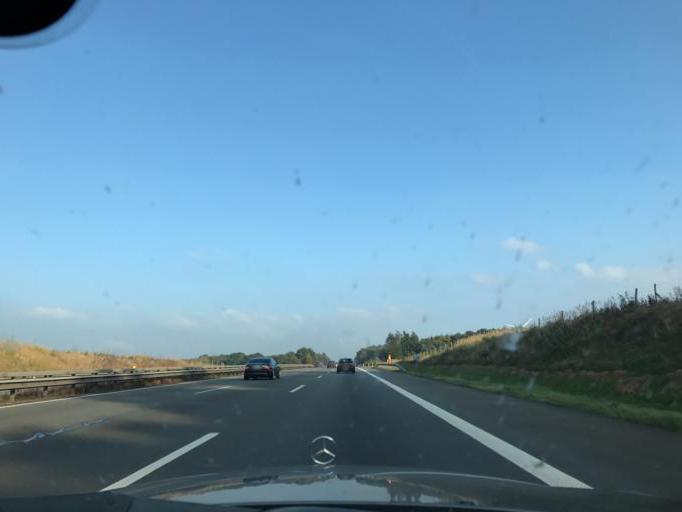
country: DE
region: Lower Saxony
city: Wenzendorf
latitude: 53.3700
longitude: 9.7703
